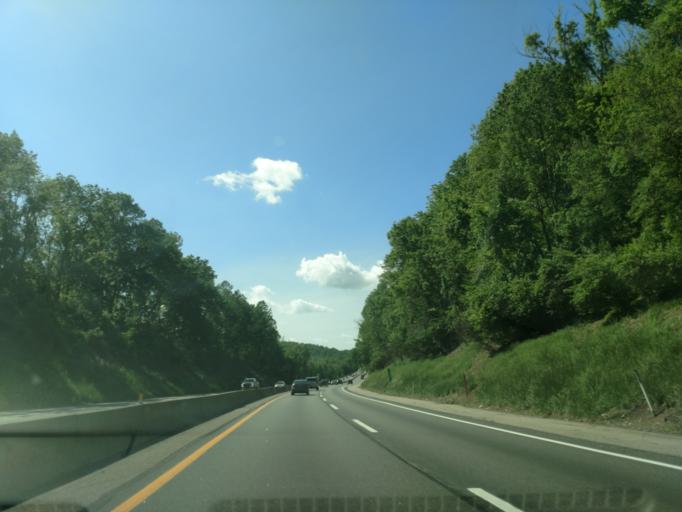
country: US
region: Pennsylvania
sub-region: Chester County
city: Downingtown
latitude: 40.0870
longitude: -75.7245
